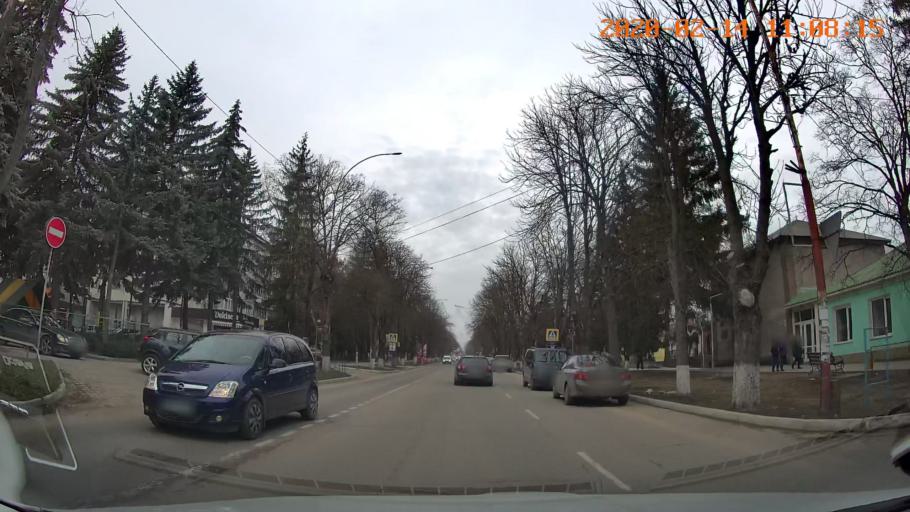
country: MD
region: Raionul Edinet
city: Edinet
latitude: 48.1712
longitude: 27.3034
